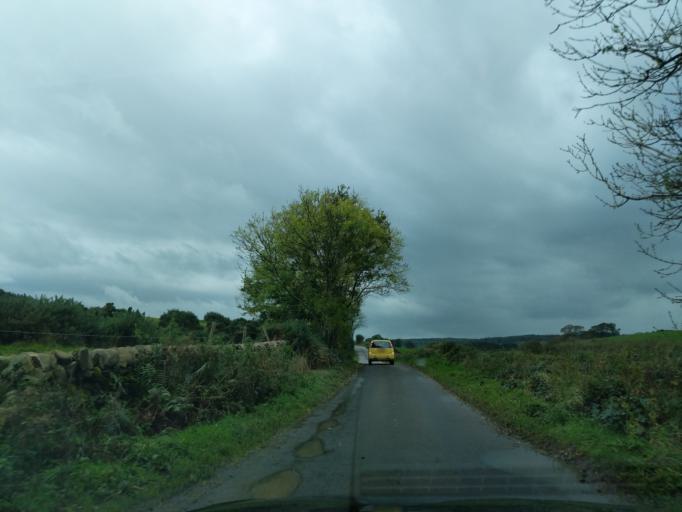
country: GB
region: Scotland
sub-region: Dumfries and Galloway
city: Castle Douglas
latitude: 54.9003
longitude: -3.9896
